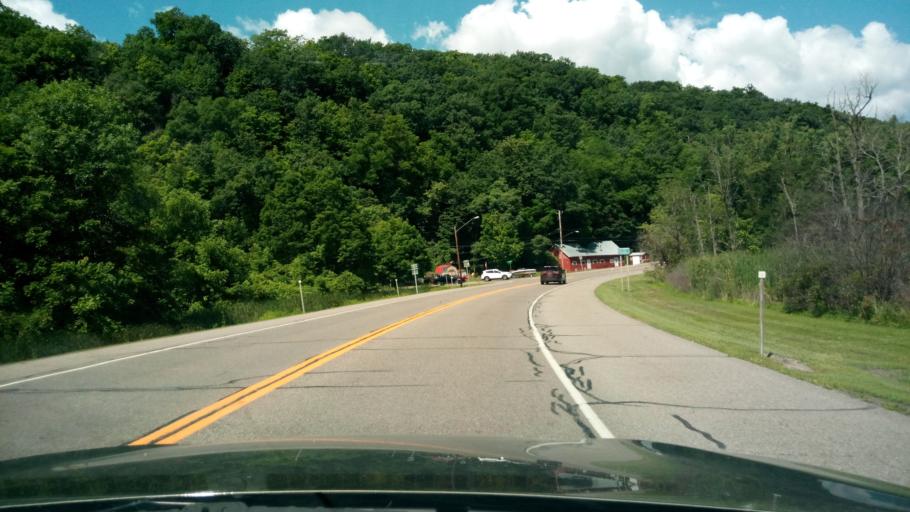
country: US
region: New York
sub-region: Schuyler County
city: Montour Falls
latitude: 42.3507
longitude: -76.8532
